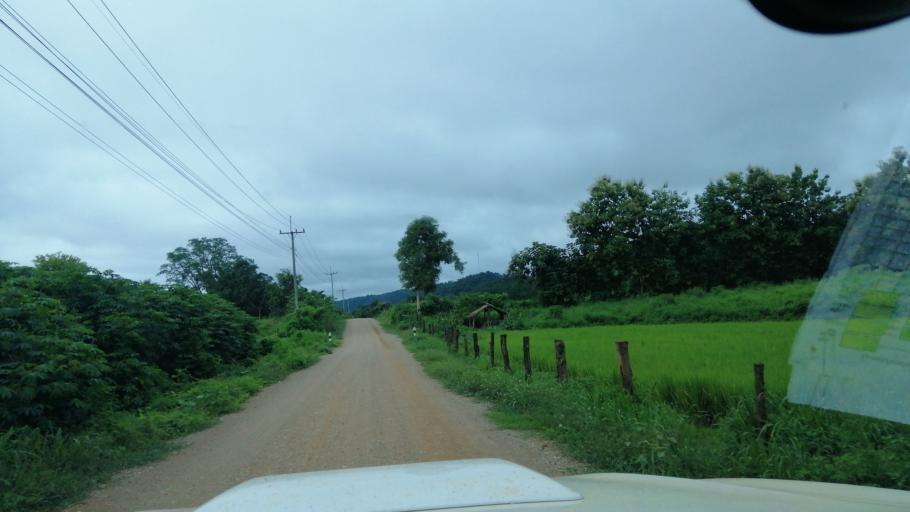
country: LA
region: Xiagnabouli
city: Muang Kenthao
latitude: 17.9589
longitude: 101.4086
